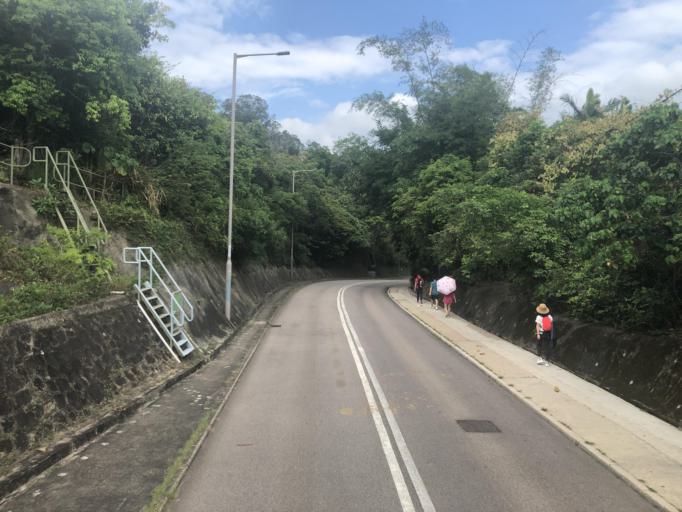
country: HK
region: Sai Kung
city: Sai Kung
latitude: 22.3931
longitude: 114.3108
